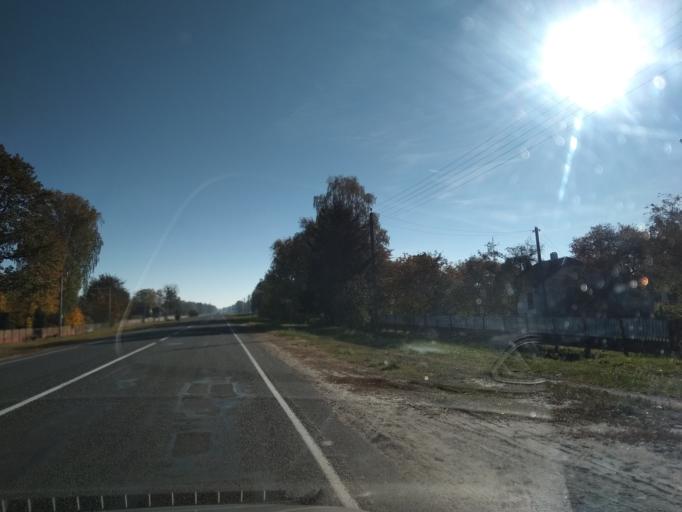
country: BY
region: Brest
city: Malaryta
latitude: 51.8332
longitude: 24.2625
